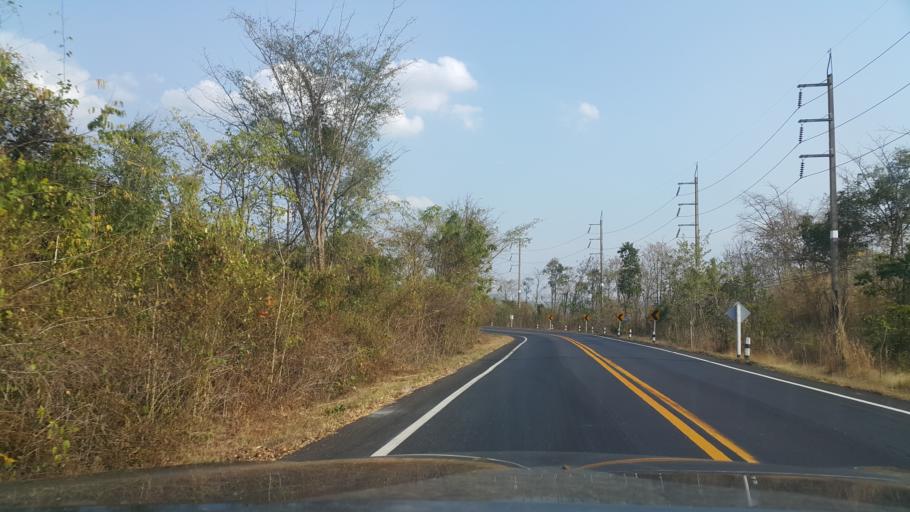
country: TH
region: Loei
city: Dan Sai
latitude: 17.1846
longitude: 100.9994
